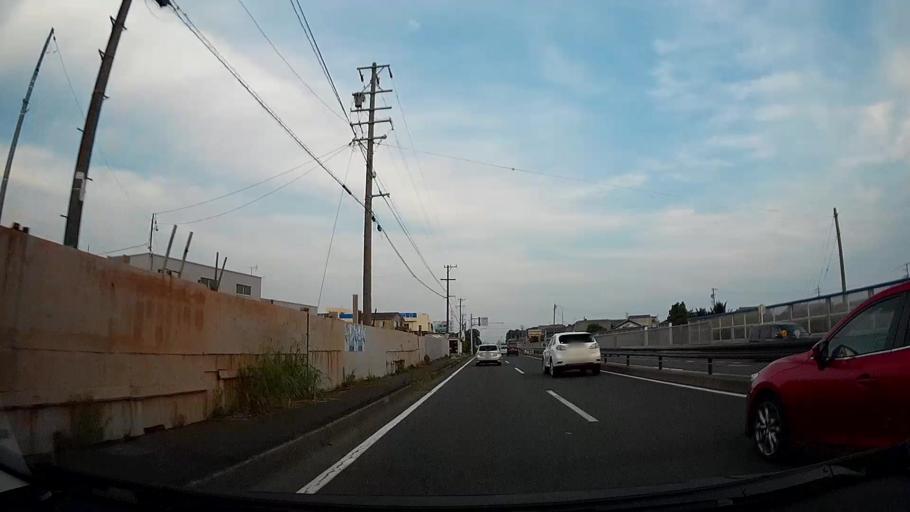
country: JP
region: Aichi
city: Kozakai-cho
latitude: 34.8024
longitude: 137.3628
